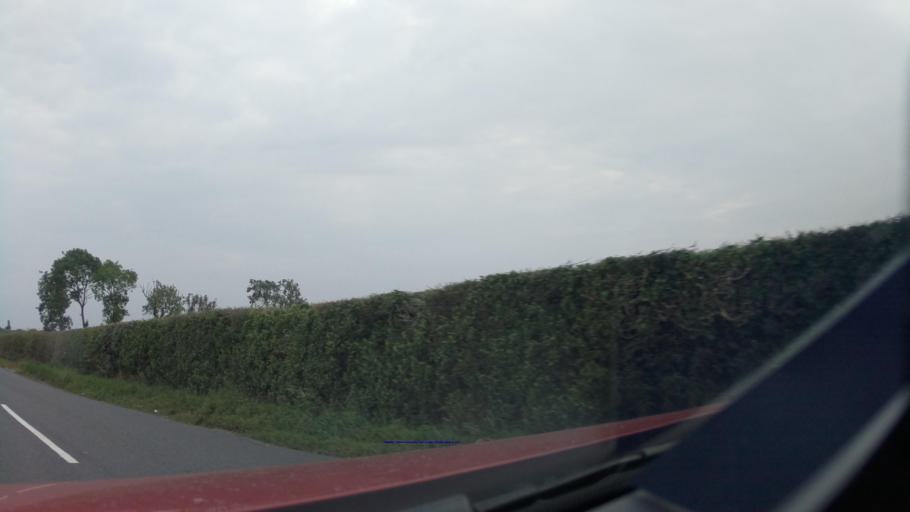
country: GB
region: England
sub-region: Lincolnshire
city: Skellingthorpe
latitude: 53.1388
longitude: -0.6456
